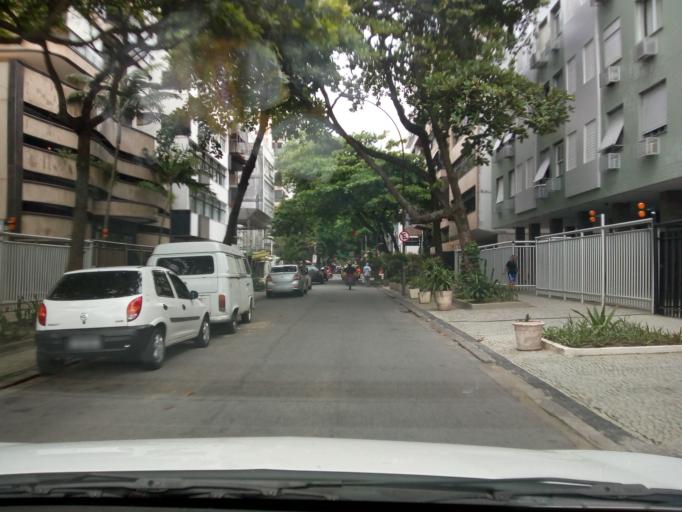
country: BR
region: Rio de Janeiro
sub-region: Rio De Janeiro
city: Rio de Janeiro
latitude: -22.9859
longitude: -43.2115
